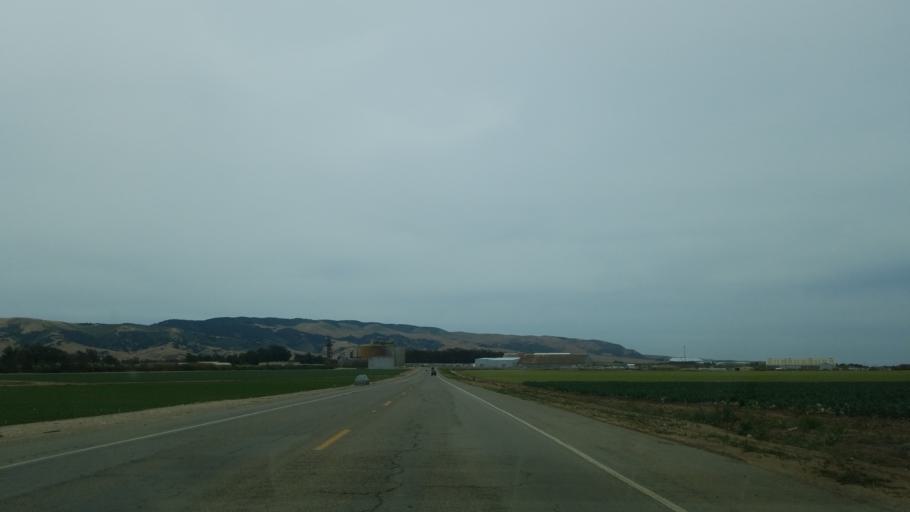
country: US
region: California
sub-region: Santa Barbara County
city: Santa Maria
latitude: 34.9195
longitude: -120.5064
